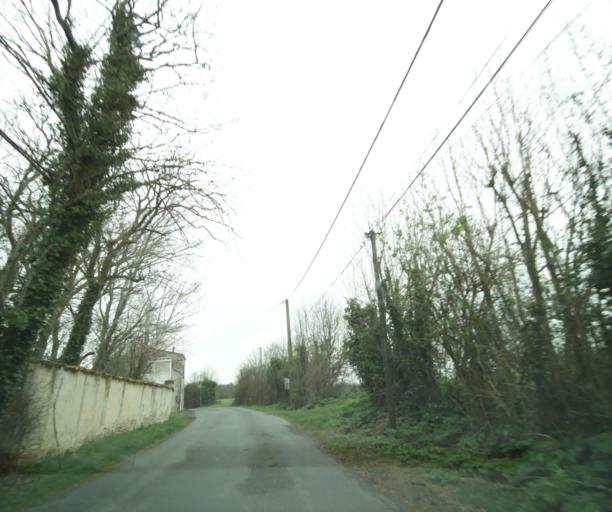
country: FR
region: Poitou-Charentes
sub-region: Departement de la Charente-Maritime
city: Lagord
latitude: 46.1839
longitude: -1.1371
